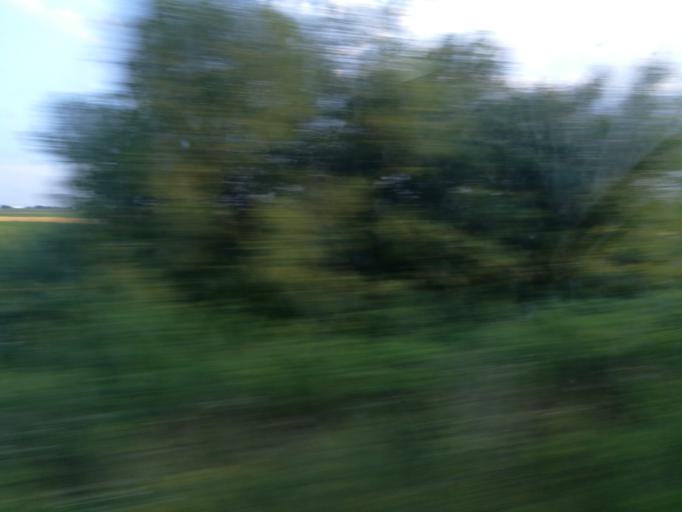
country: RO
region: Dambovita
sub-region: Comuna Titu
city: Salcuta
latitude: 44.6612
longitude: 25.5909
